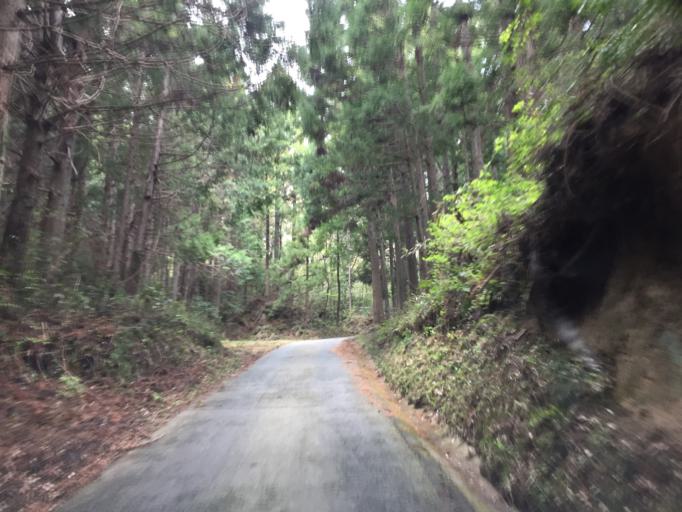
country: JP
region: Fukushima
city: Iwaki
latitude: 37.1412
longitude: 140.9037
